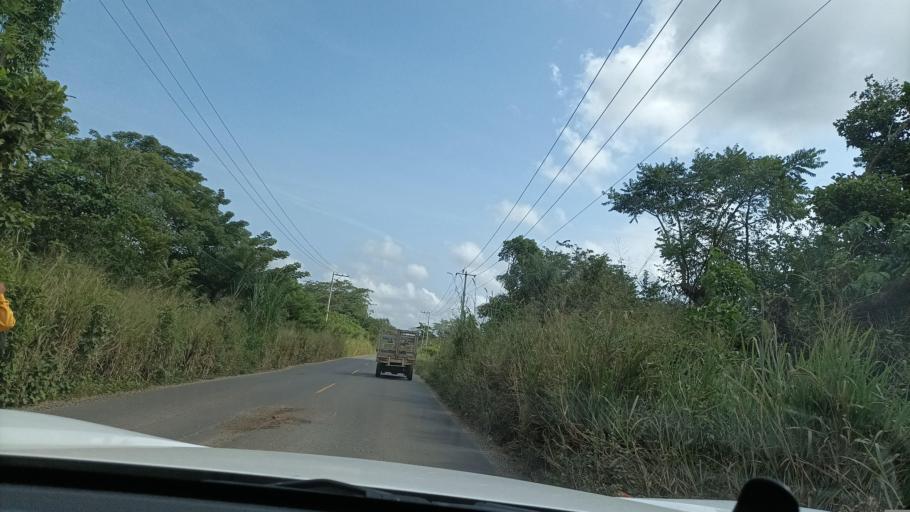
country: MX
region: Veracruz
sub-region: Chinameca
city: Chacalapa
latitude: 18.0701
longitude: -94.6848
